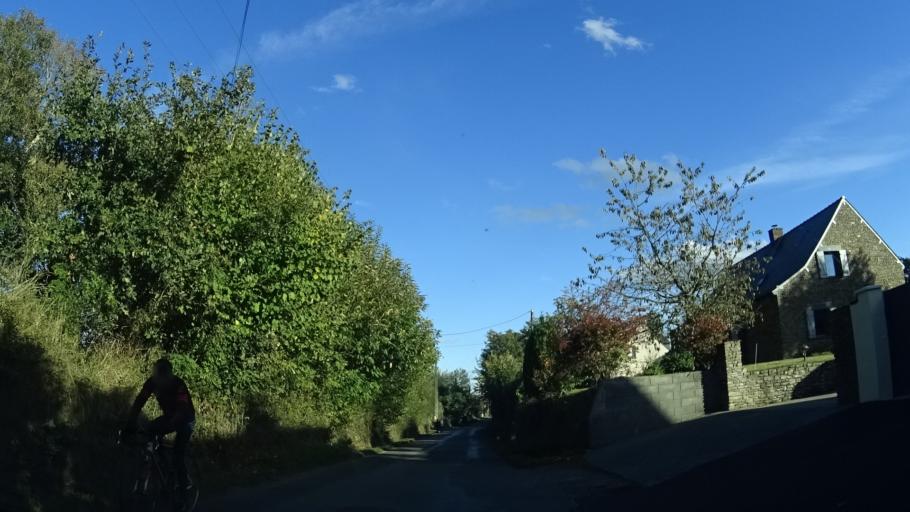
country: FR
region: Brittany
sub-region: Departement d'Ille-et-Vilaine
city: Le Minihic-sur-Rance
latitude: 48.5835
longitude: -2.0149
